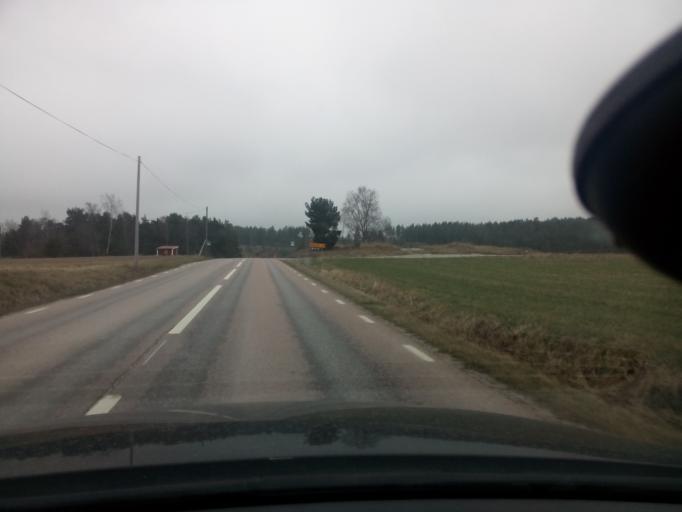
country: SE
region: Soedermanland
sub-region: Gnesta Kommun
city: Gnesta
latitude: 59.0502
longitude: 17.1556
